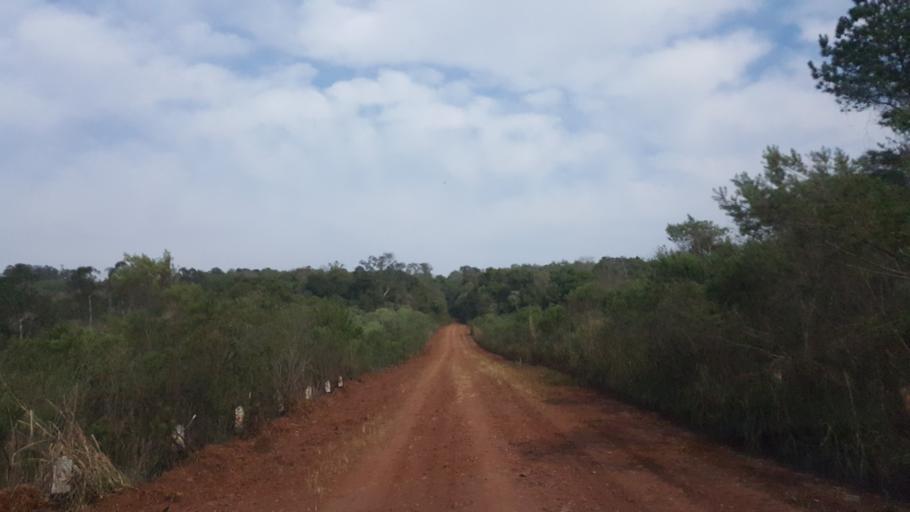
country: AR
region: Misiones
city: Capiovi
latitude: -26.9029
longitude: -55.1101
